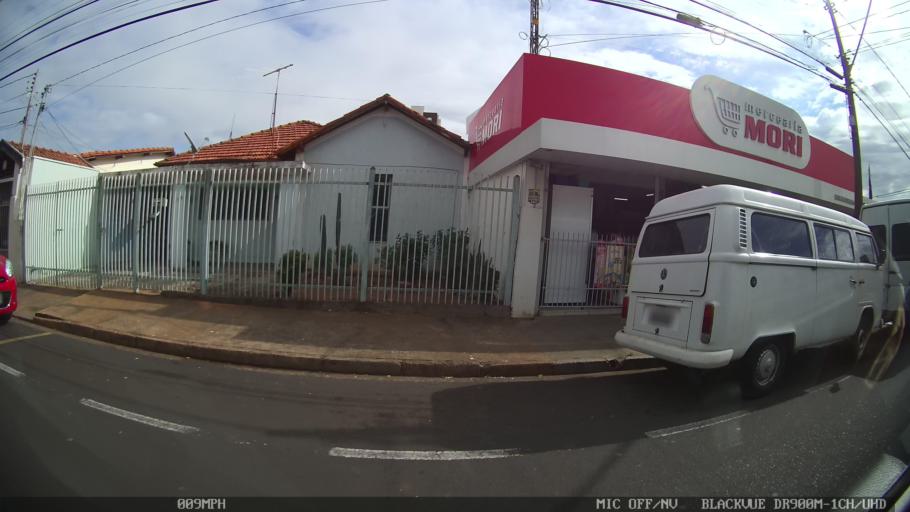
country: BR
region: Sao Paulo
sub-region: Sao Jose Do Rio Preto
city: Sao Jose do Rio Preto
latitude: -20.8197
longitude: -49.3749
